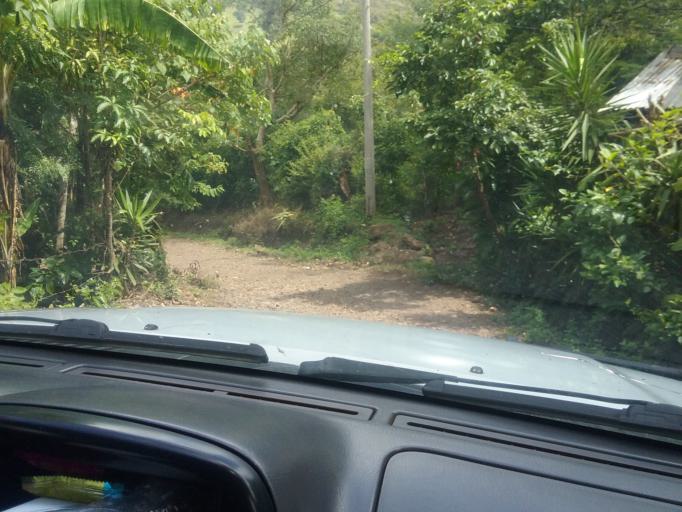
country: NI
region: Matagalpa
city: Matagalpa
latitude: 12.8670
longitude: -85.9150
